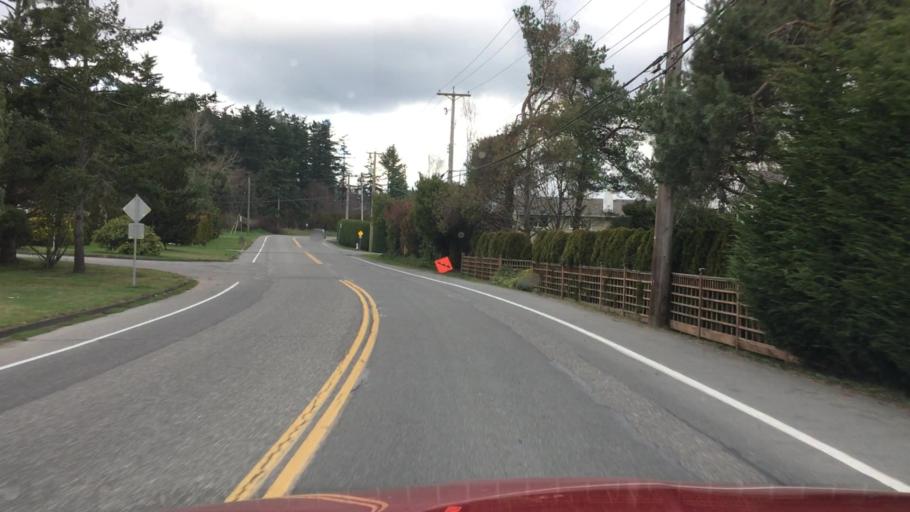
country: CA
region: British Columbia
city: North Saanich
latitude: 48.5997
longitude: -123.3948
